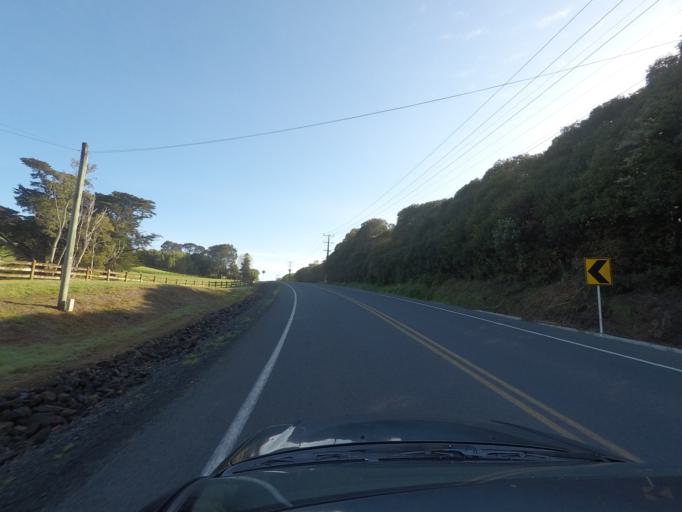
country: NZ
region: Auckland
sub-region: Auckland
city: Red Hill
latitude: -36.9948
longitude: 174.9842
